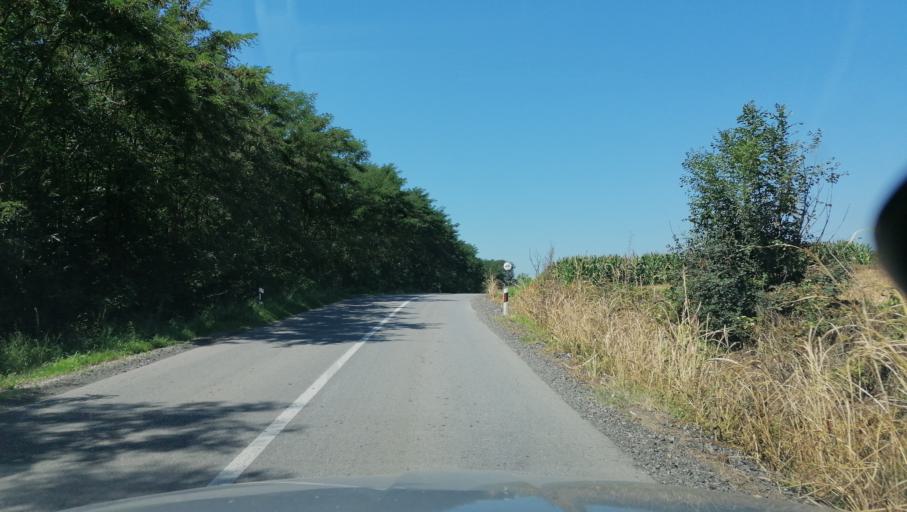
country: RS
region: Central Serbia
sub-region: Raski Okrug
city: Vrnjacka Banja
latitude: 43.7162
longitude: 20.8232
